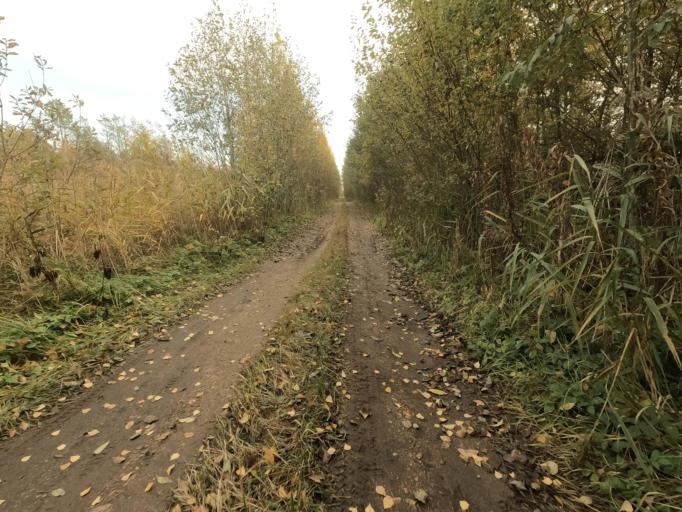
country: RU
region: Novgorod
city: Pankovka
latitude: 58.8792
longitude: 30.8539
